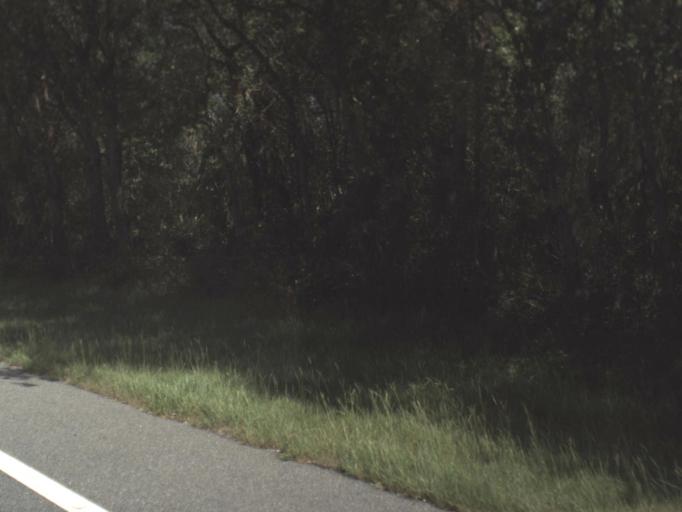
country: US
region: Florida
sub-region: Putnam County
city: Interlachen
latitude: 29.7131
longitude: -81.7970
